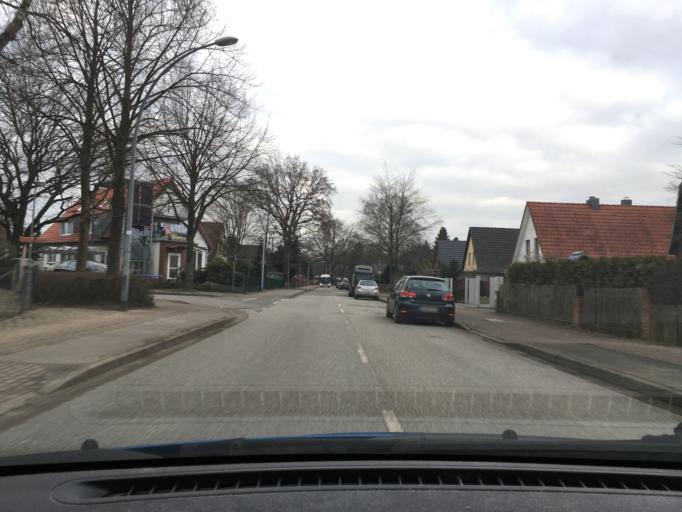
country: DE
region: Schleswig-Holstein
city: Wedel
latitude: 53.5949
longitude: 9.7247
